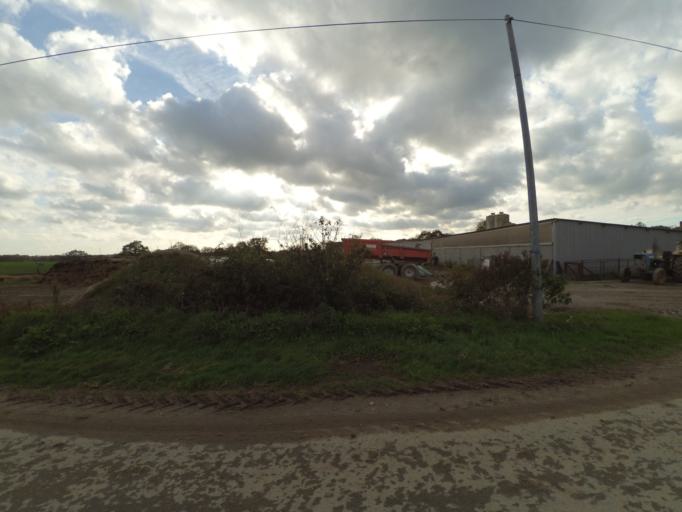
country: FR
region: Pays de la Loire
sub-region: Departement de la Vendee
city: Saint-Hilaire-de-Loulay
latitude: 47.0164
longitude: -1.3563
